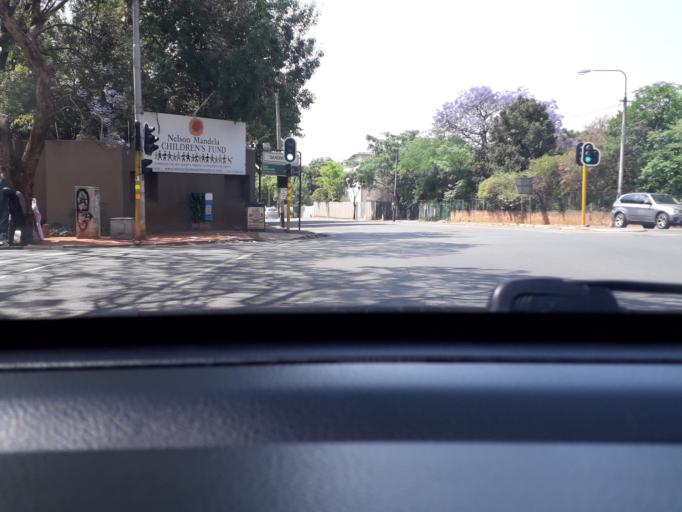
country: ZA
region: Gauteng
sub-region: City of Johannesburg Metropolitan Municipality
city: Johannesburg
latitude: -26.1650
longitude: 28.0479
